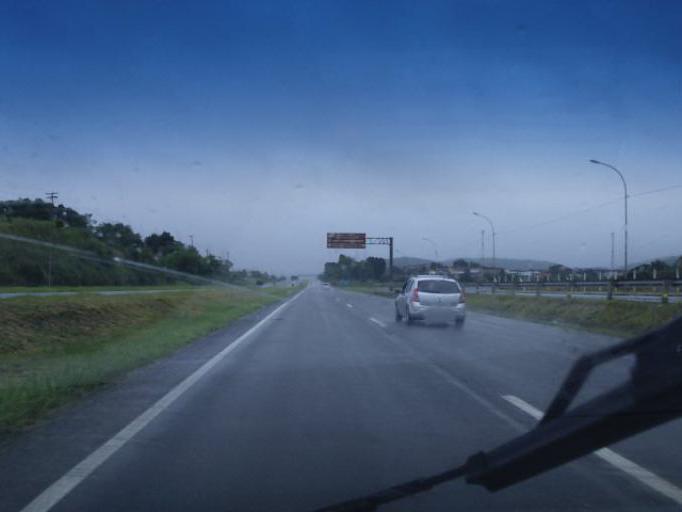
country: BR
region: Sao Paulo
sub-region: Jacupiranga
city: Jacupiranga
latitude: -24.7075
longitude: -48.0157
